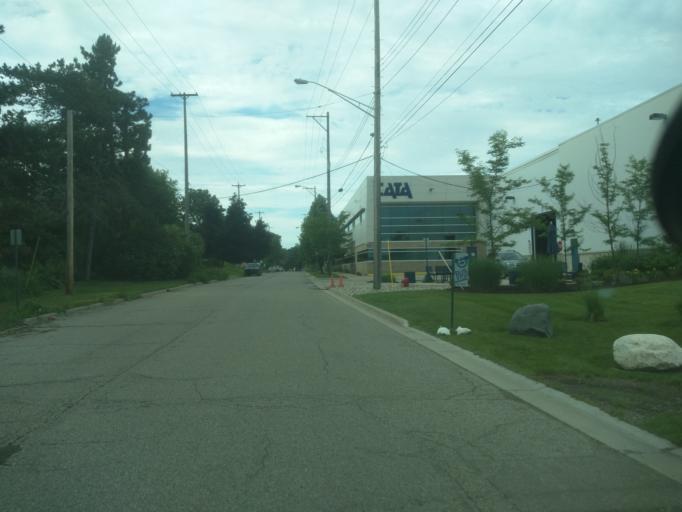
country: US
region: Michigan
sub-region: Ingham County
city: Holt
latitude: 42.6863
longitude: -84.5346
